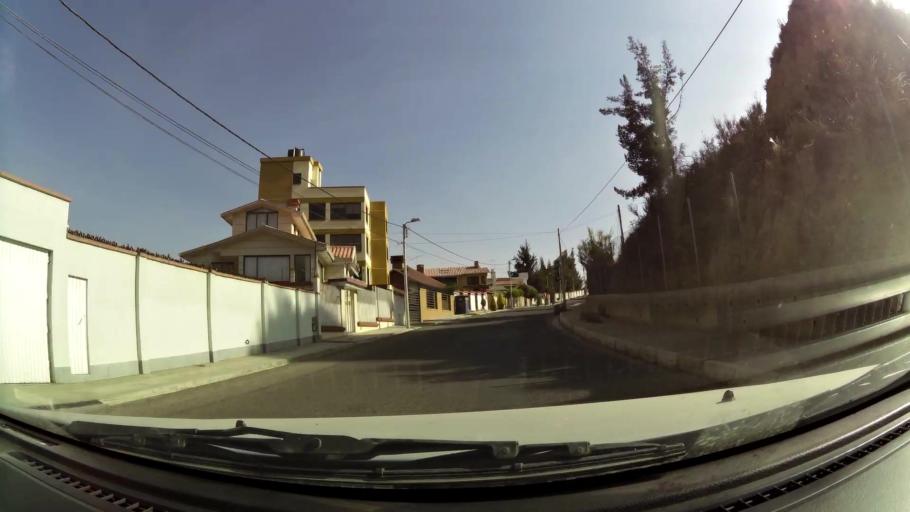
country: BO
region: La Paz
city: La Paz
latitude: -16.5303
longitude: -68.0755
